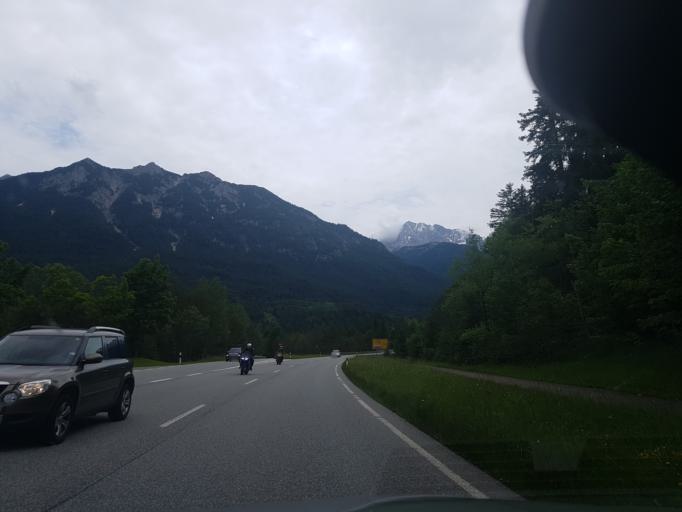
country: DE
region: Bavaria
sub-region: Upper Bavaria
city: Krun
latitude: 47.4996
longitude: 11.2716
